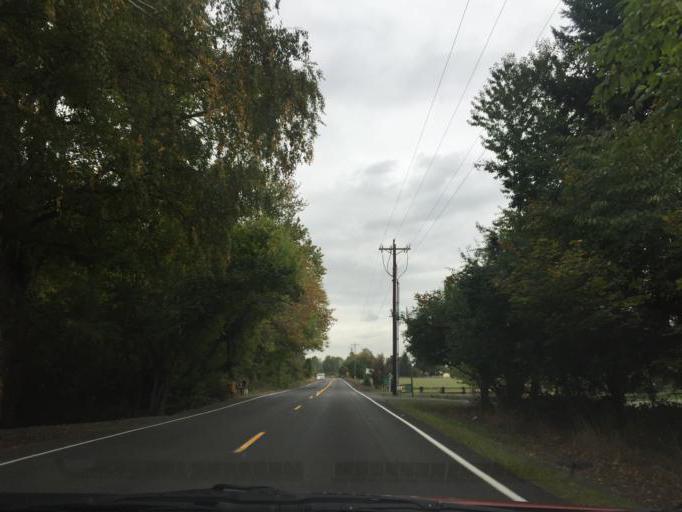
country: US
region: Oregon
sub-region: Washington County
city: Oak Hills
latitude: 45.6304
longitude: -122.8021
